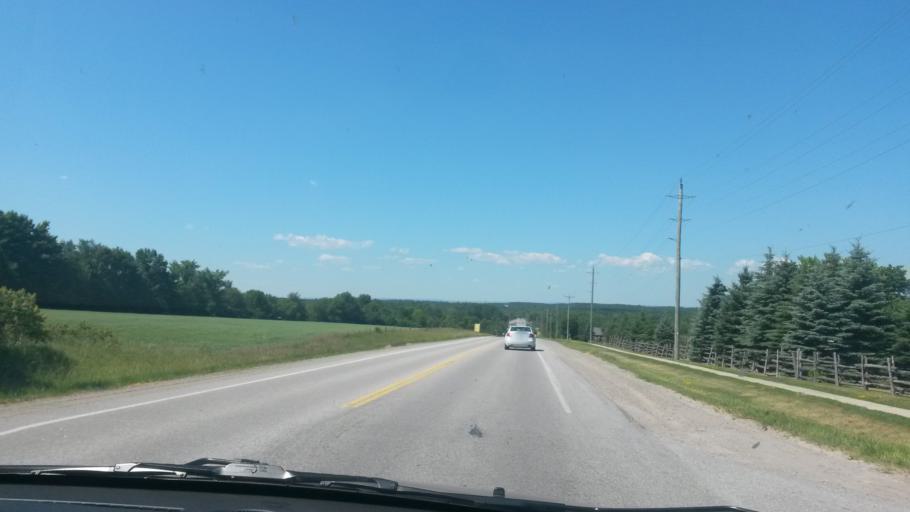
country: CA
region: Ontario
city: Barrie
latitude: 44.5283
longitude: -79.7290
